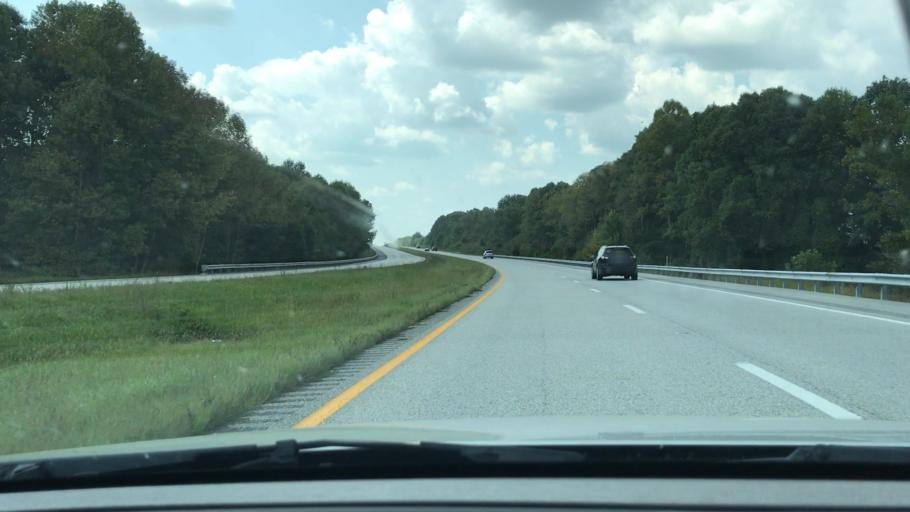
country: US
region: Kentucky
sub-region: Russell County
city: Russell Springs
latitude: 37.0882
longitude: -84.9142
